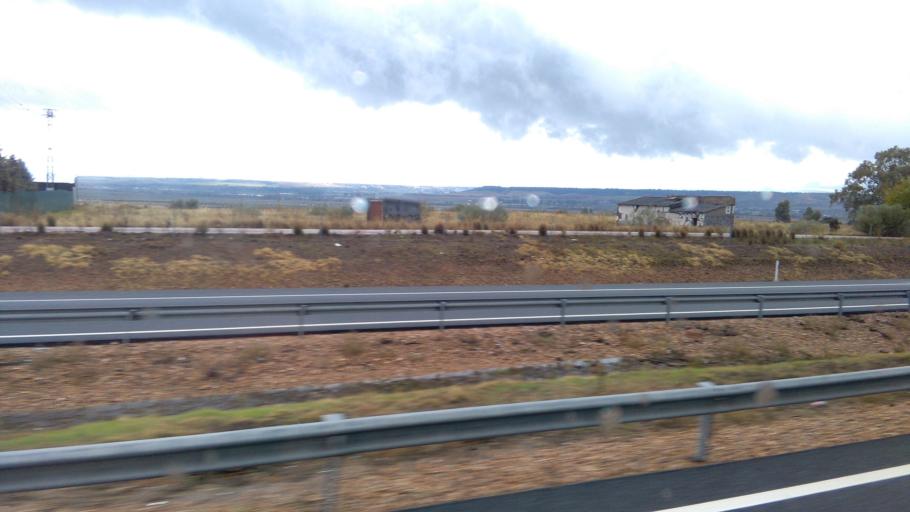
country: ES
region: Castille-La Mancha
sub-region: Province of Toledo
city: Cazalegas
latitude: 39.9925
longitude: -4.6940
